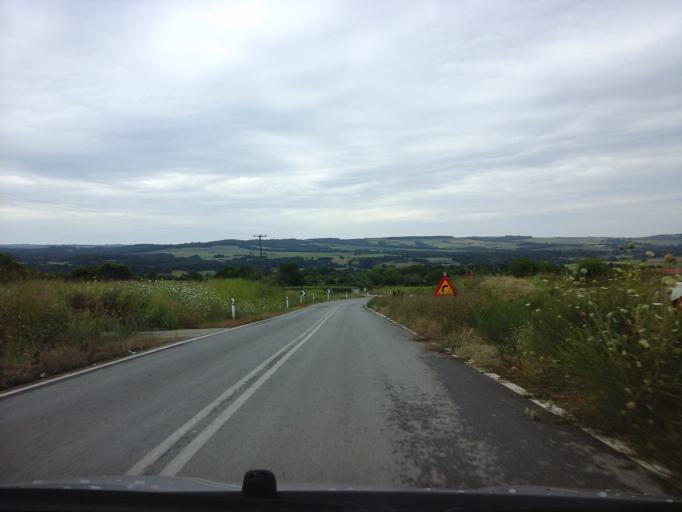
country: GR
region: East Macedonia and Thrace
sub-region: Nomos Evrou
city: Soufli
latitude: 41.1315
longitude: 26.2330
